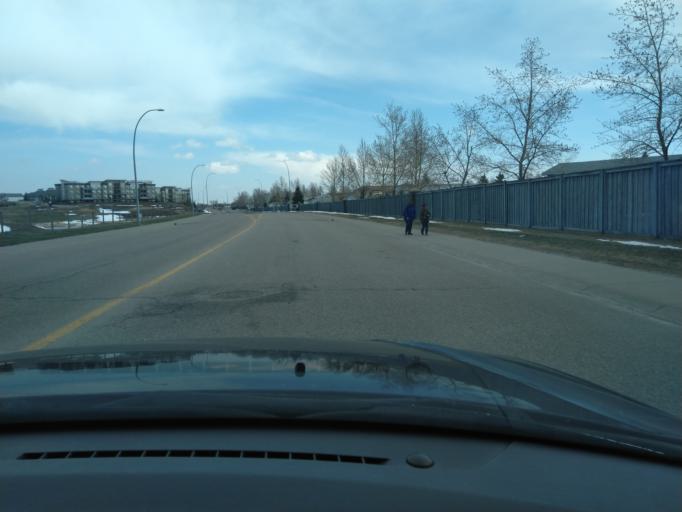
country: CA
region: Alberta
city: Calgary
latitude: 51.1295
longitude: -114.2158
